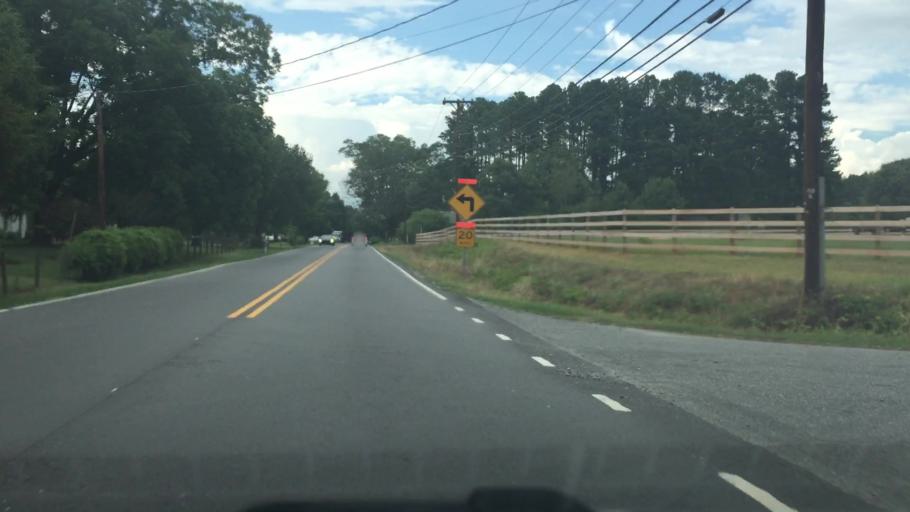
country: US
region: North Carolina
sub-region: Rowan County
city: Enochville
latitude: 35.4586
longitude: -80.7323
